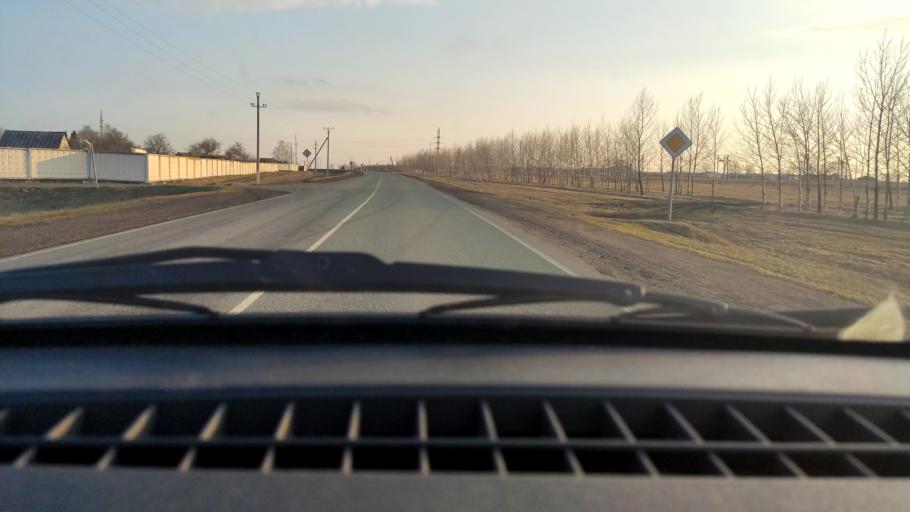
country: RU
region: Bashkortostan
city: Davlekanovo
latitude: 54.3865
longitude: 55.1989
